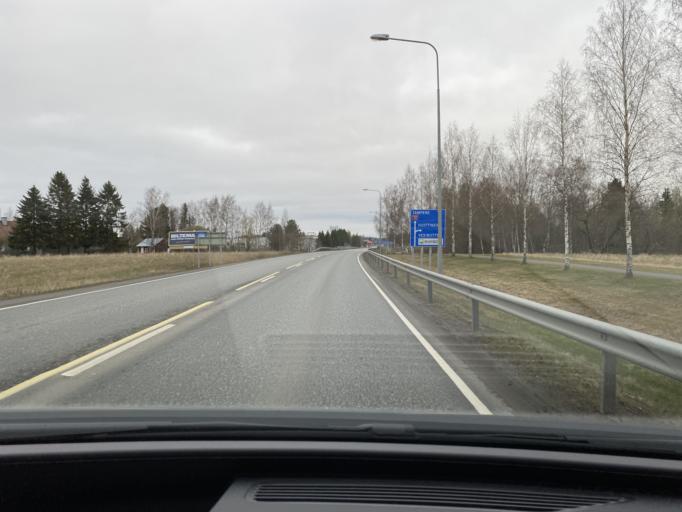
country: FI
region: Satakunta
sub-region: Pori
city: Huittinen
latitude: 61.1854
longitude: 22.6856
